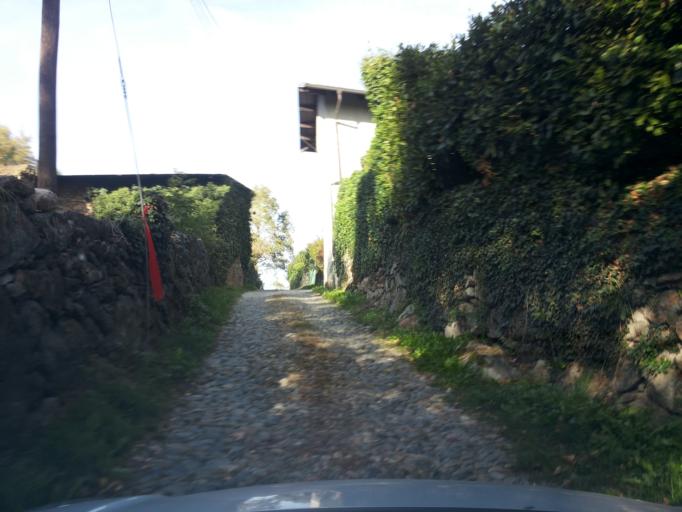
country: IT
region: Piedmont
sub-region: Provincia di Biella
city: Roppolo
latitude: 45.4346
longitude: 8.0749
